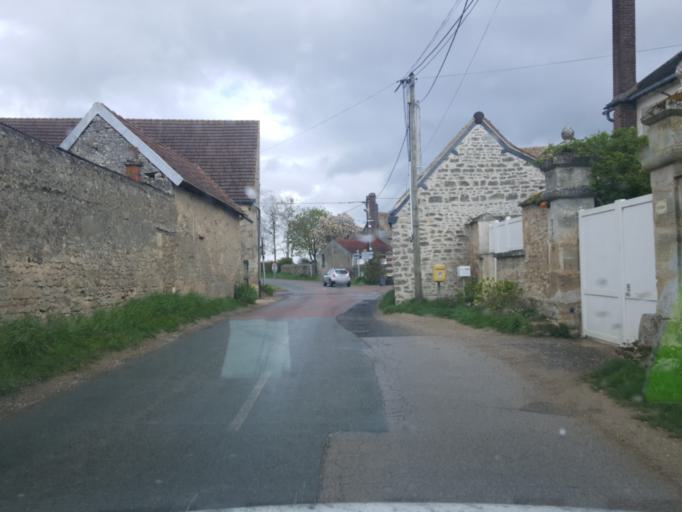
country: FR
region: Picardie
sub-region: Departement de l'Oise
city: Trie-Chateau
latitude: 49.2207
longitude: 1.8072
